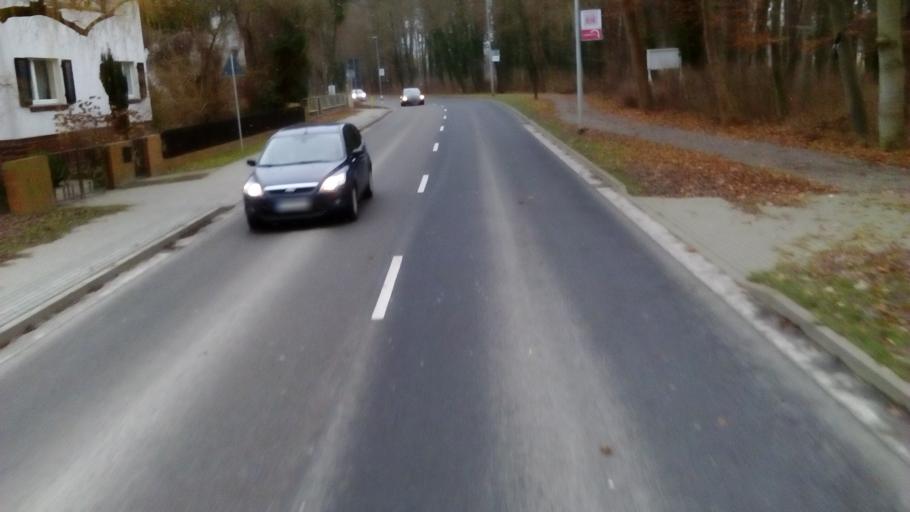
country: DE
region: Mecklenburg-Vorpommern
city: Strasburg
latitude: 53.5039
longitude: 13.7539
